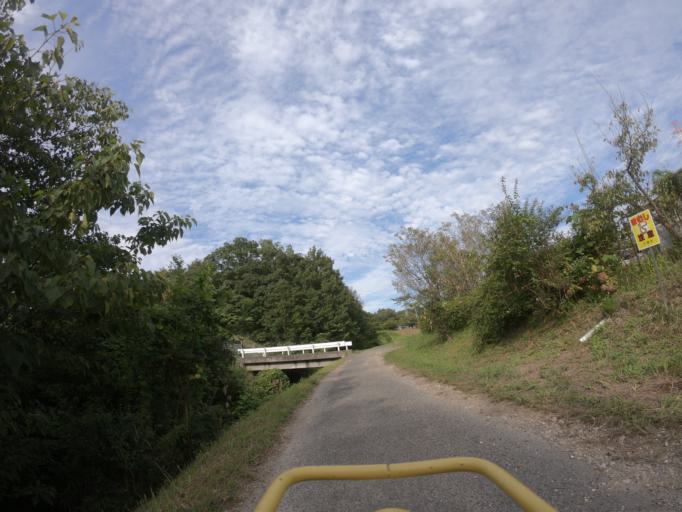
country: JP
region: Aichi
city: Seto
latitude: 35.1476
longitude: 137.0888
